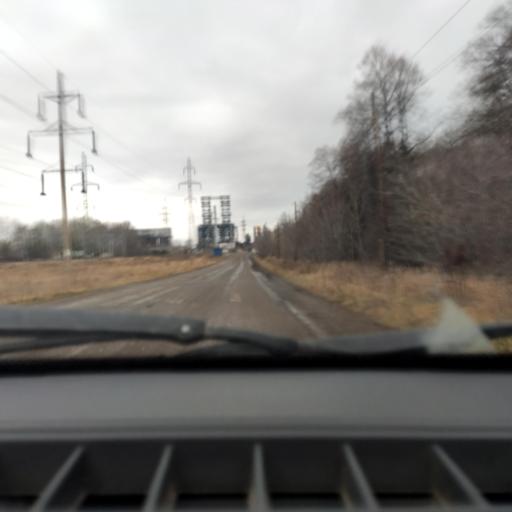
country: RU
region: Bashkortostan
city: Blagoveshchensk
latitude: 54.9390
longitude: 56.0829
